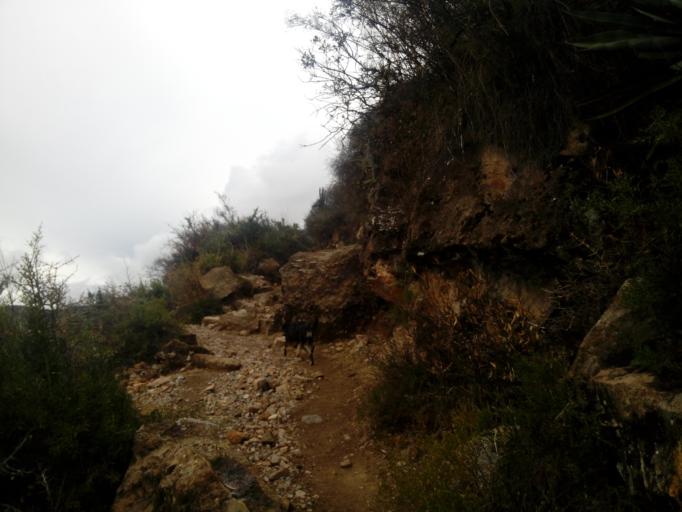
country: PE
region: Ayacucho
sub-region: Provincia de Victor Fajardo
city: Canaria
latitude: -13.8988
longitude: -73.9330
